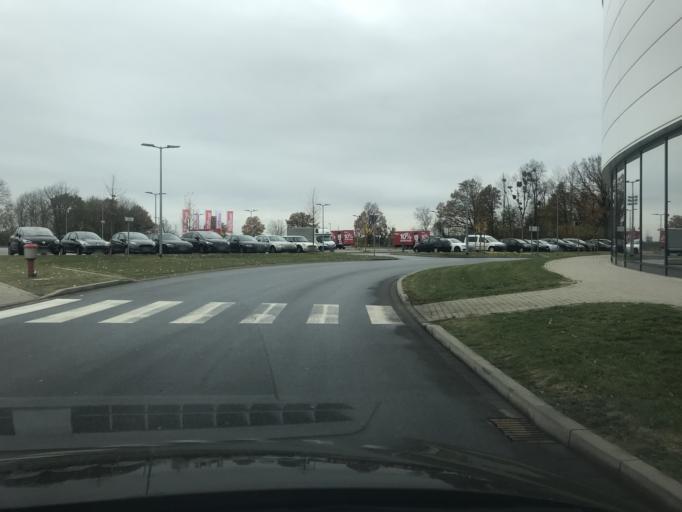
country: DE
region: North Rhine-Westphalia
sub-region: Regierungsbezirk Arnsberg
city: Hamm
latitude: 51.6273
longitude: 7.8431
